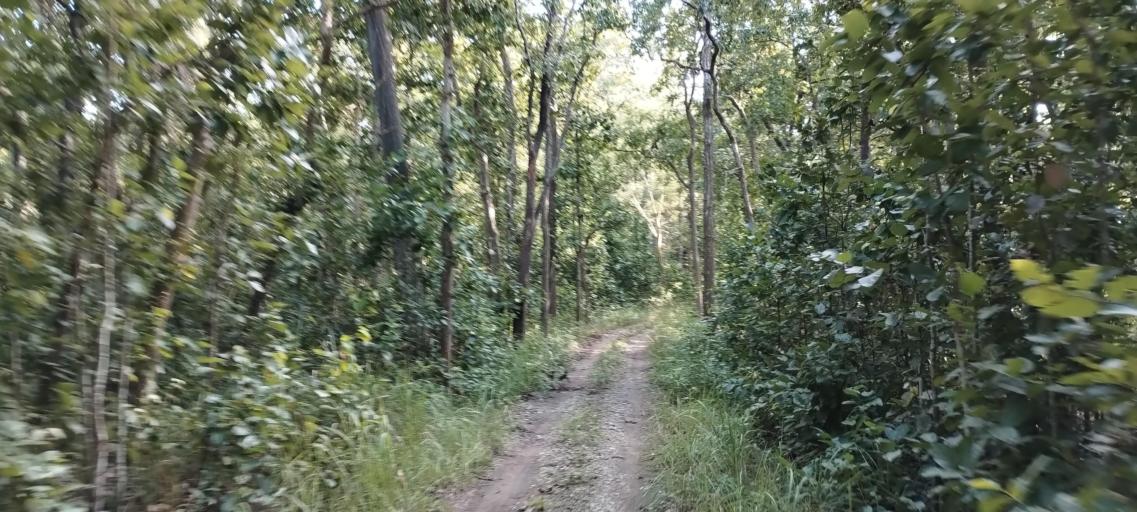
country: NP
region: Far Western
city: Tikapur
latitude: 28.5395
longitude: 81.2863
